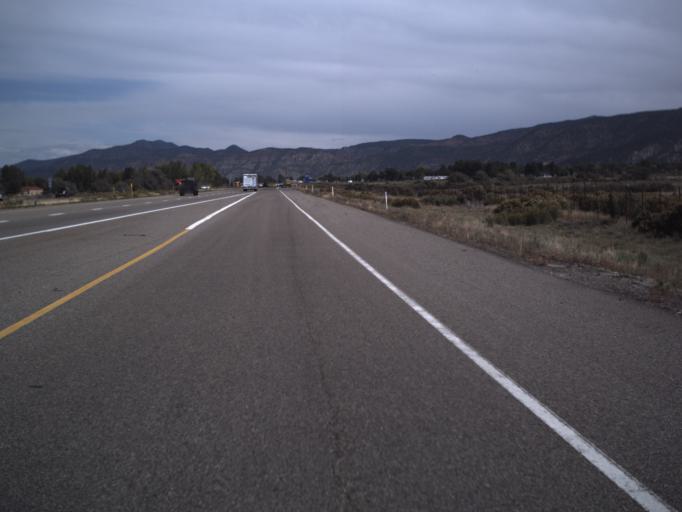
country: US
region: Utah
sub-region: Iron County
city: Parowan
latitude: 37.8404
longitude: -112.8653
